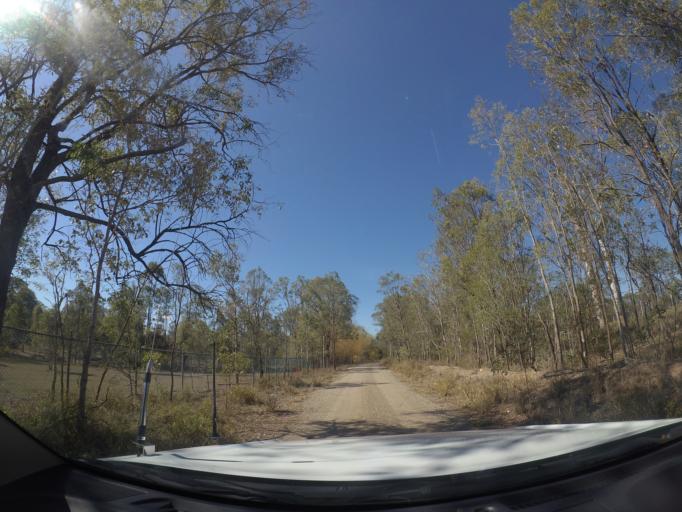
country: AU
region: Queensland
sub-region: Logan
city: North Maclean
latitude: -27.7720
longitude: 153.0148
